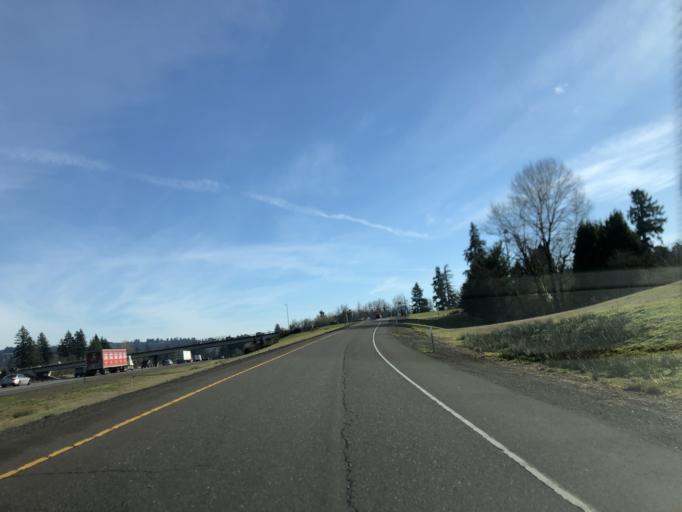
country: US
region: Oregon
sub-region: Clackamas County
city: Stafford
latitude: 45.3708
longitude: -122.7099
